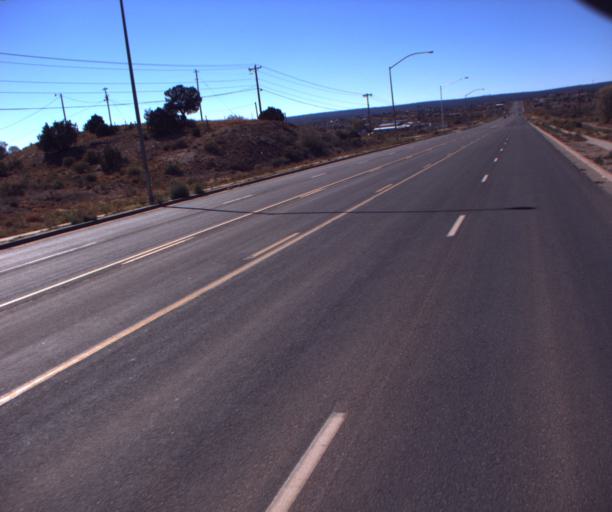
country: US
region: Arizona
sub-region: Apache County
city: Window Rock
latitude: 35.6607
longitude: -109.0719
